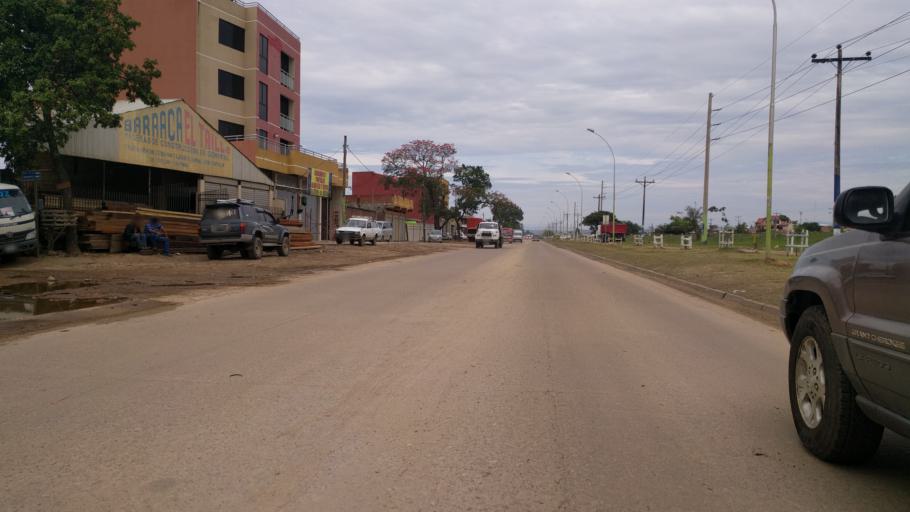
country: BO
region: Santa Cruz
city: Santa Cruz de la Sierra
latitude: -17.8434
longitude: -63.1734
